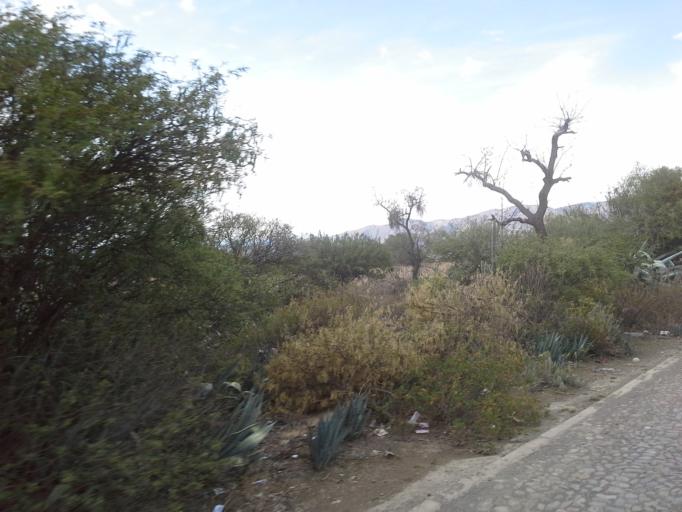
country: BO
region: Cochabamba
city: Tarata
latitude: -17.6055
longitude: -66.0214
